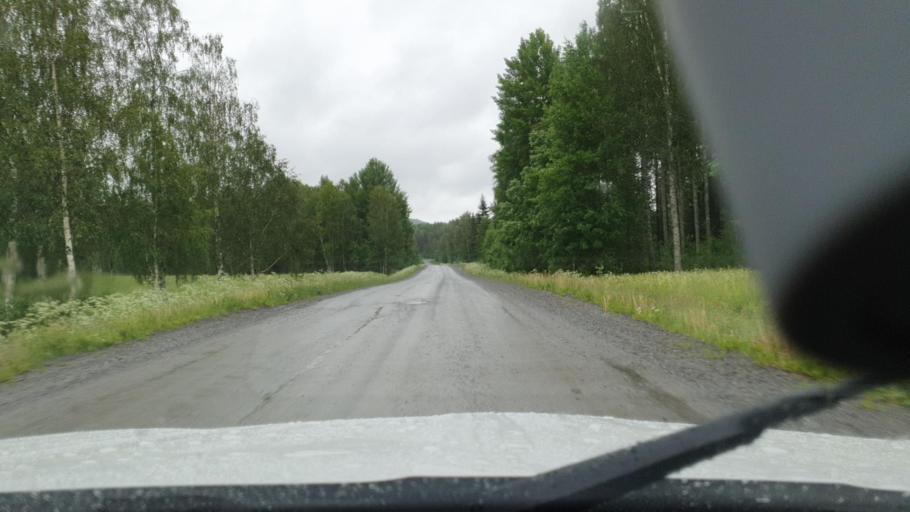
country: SE
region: Vaesterbotten
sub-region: Skelleftea Kommun
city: Burtraesk
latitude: 64.3654
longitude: 20.4043
